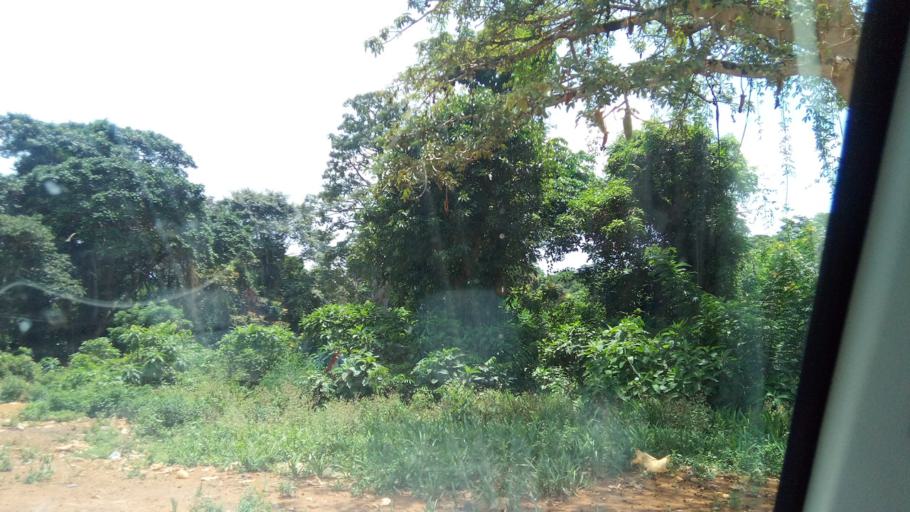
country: AO
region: Zaire
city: Mbanza Congo
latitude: -5.8140
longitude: 14.2458
